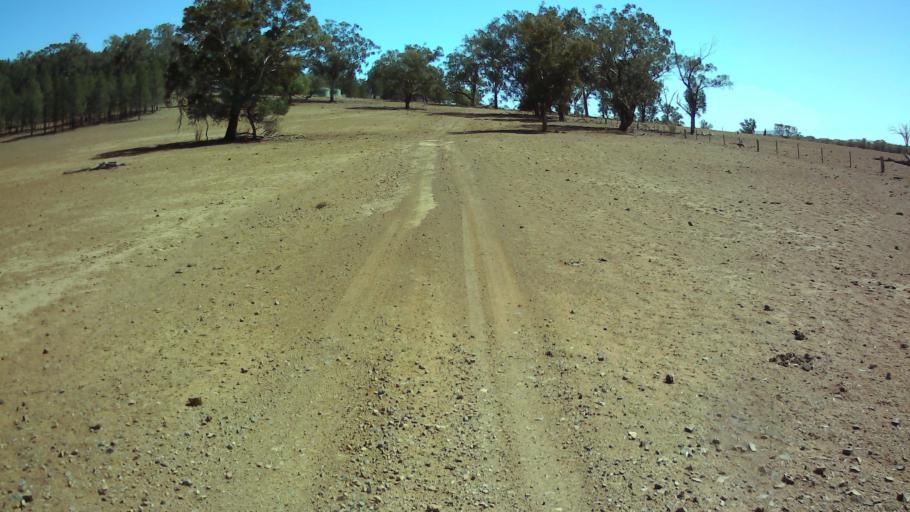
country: AU
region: New South Wales
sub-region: Forbes
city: Forbes
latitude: -33.7336
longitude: 147.6639
